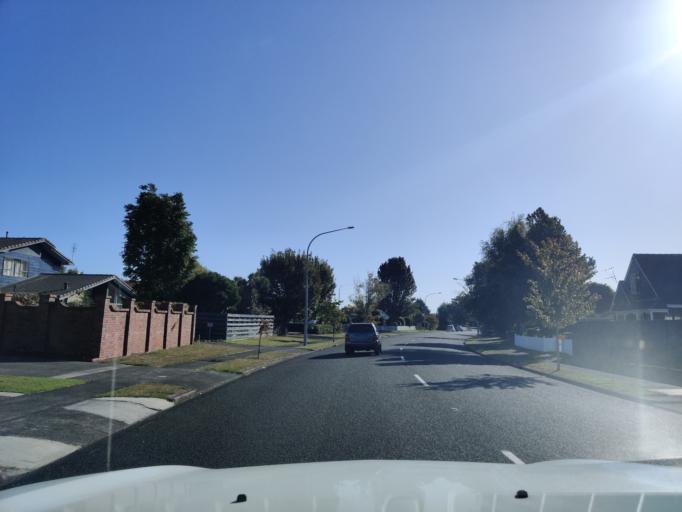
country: NZ
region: Auckland
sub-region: Auckland
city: Takanini
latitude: -37.0436
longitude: 174.9174
